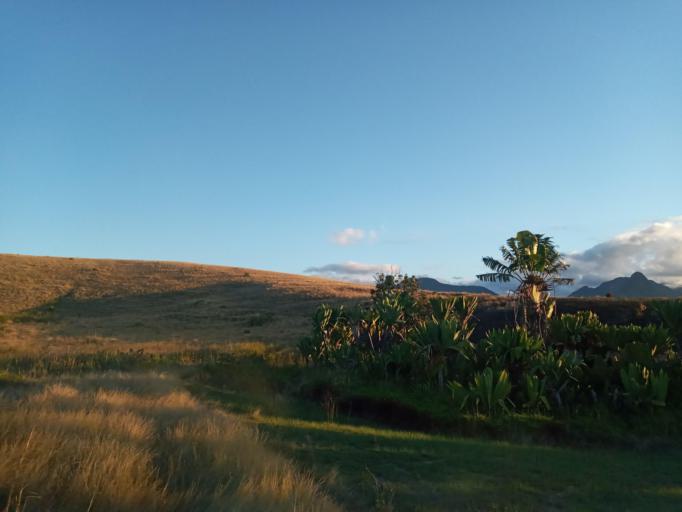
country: MG
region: Anosy
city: Fort Dauphin
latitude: -24.5137
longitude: 47.2505
